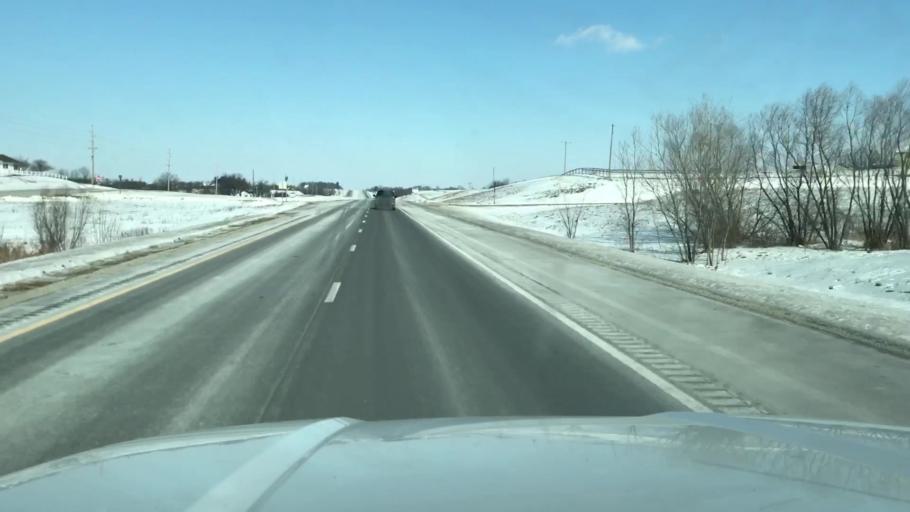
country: US
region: Missouri
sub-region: Nodaway County
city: Maryville
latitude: 40.1849
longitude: -94.8679
